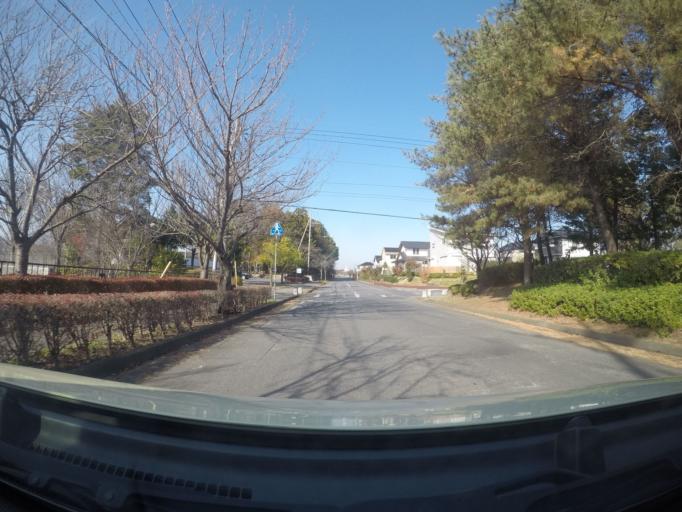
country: JP
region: Ibaraki
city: Naka
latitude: 36.1089
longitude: 140.1133
